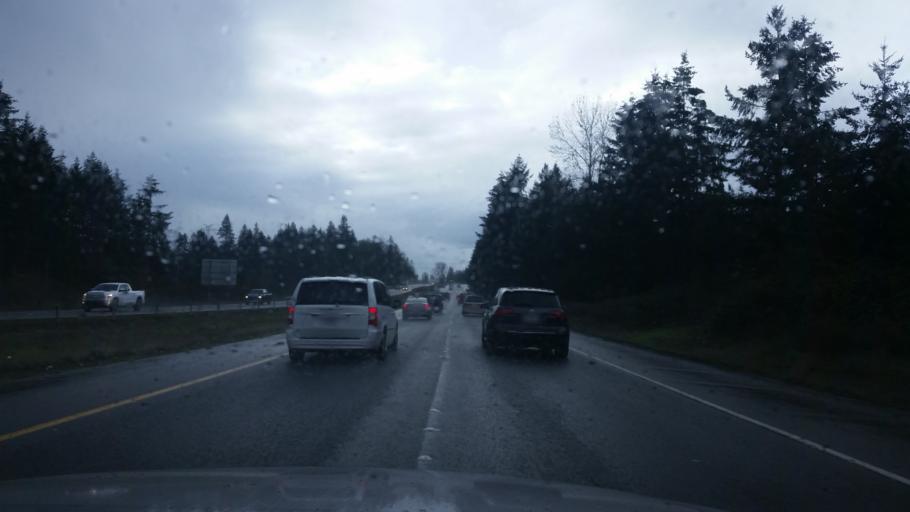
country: US
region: Washington
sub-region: King County
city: Covington
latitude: 47.3500
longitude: -122.1355
